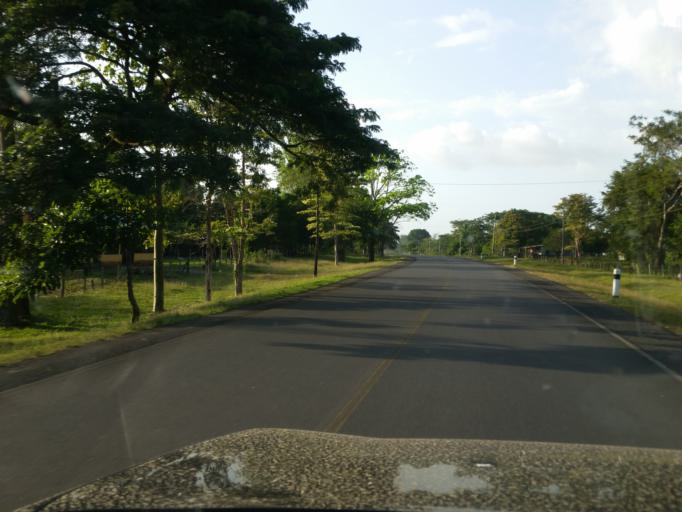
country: NI
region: Rio San Juan
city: San Miguelito
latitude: 11.3171
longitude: -84.7327
